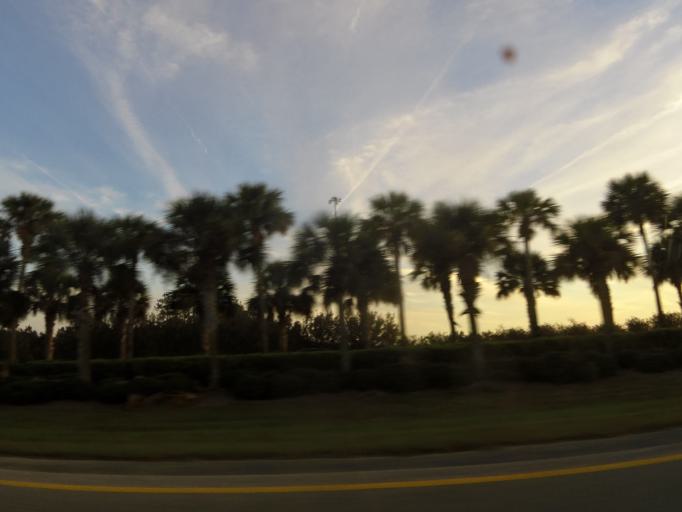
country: US
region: Florida
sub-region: Saint Johns County
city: Palm Valley
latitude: 30.1151
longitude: -81.4153
